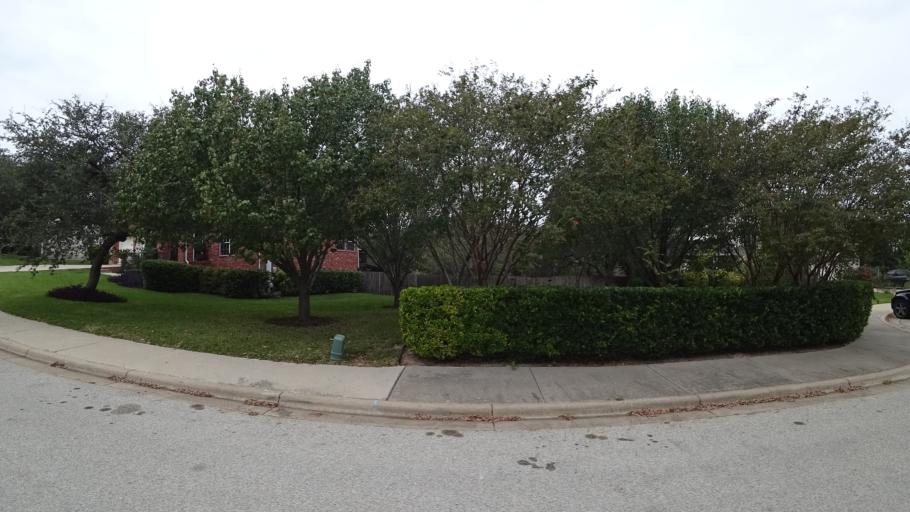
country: US
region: Texas
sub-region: Travis County
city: Bee Cave
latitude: 30.3101
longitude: -97.9298
